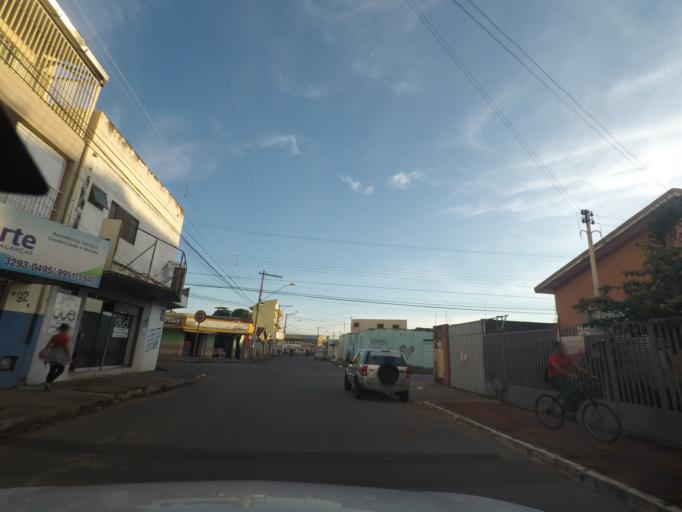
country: BR
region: Goias
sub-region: Goiania
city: Goiania
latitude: -16.6768
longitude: -49.2893
